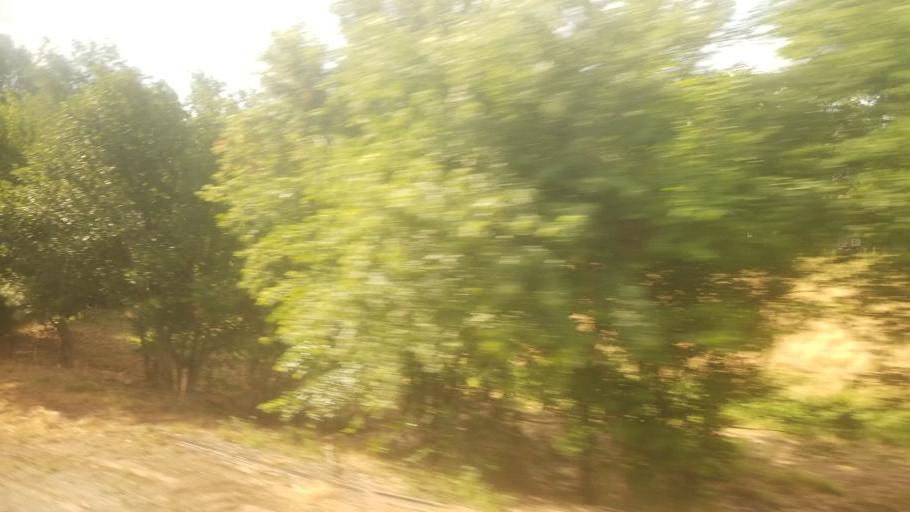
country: US
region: Kansas
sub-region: Johnson County
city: De Soto
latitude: 38.9807
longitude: -94.9359
